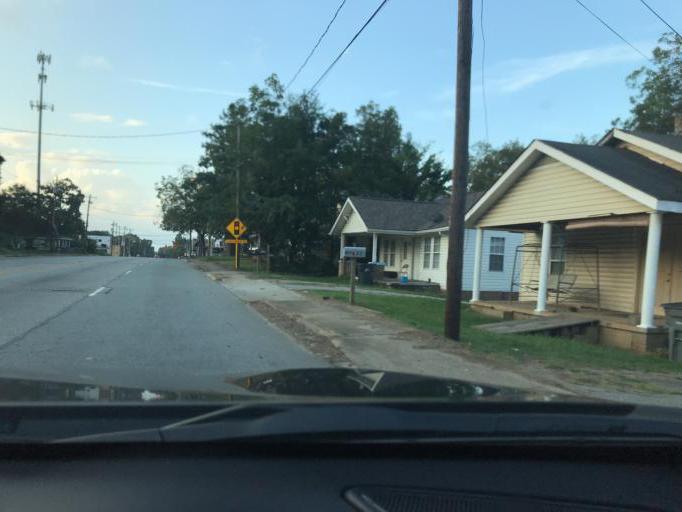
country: US
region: South Carolina
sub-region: Greenville County
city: Welcome
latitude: 34.8372
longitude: -82.4420
